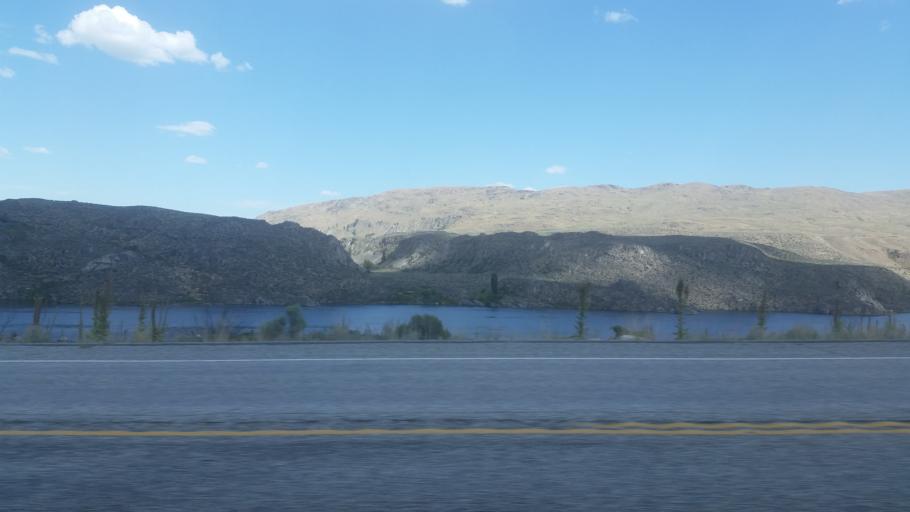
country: US
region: Washington
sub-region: Okanogan County
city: Brewster
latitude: 48.0359
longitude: -119.8950
